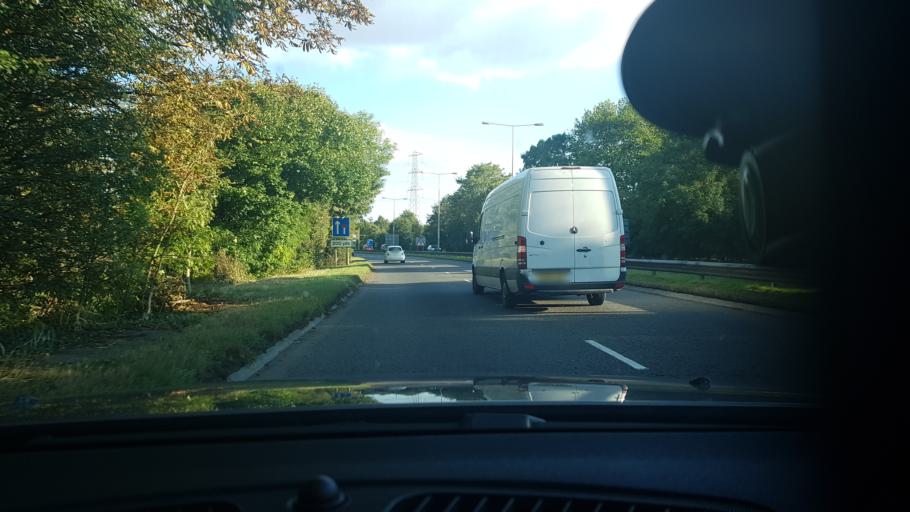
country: GB
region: England
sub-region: Gloucestershire
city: Cirencester
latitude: 51.7076
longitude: -1.9524
